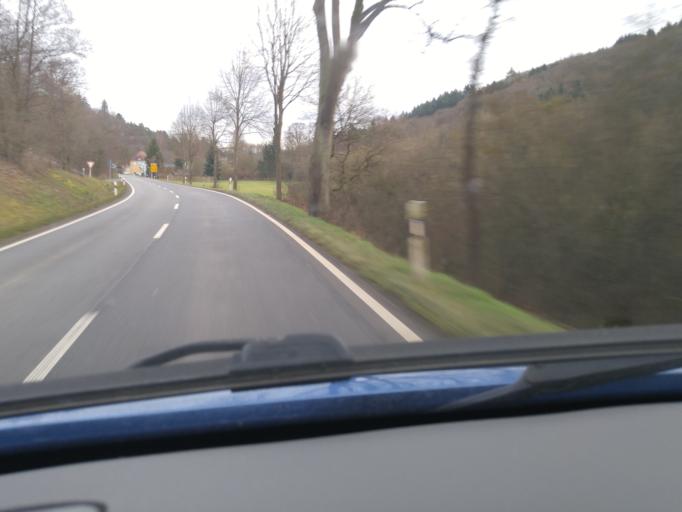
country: DE
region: Hesse
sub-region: Regierungsbezirk Darmstadt
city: Ober-Morlen
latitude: 50.3667
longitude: 8.6192
